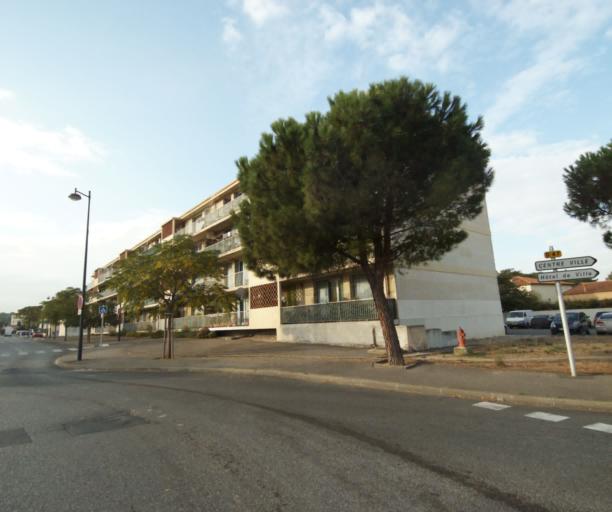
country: FR
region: Provence-Alpes-Cote d'Azur
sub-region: Departement des Bouches-du-Rhone
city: Saint-Victoret
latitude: 43.4187
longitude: 5.2451
